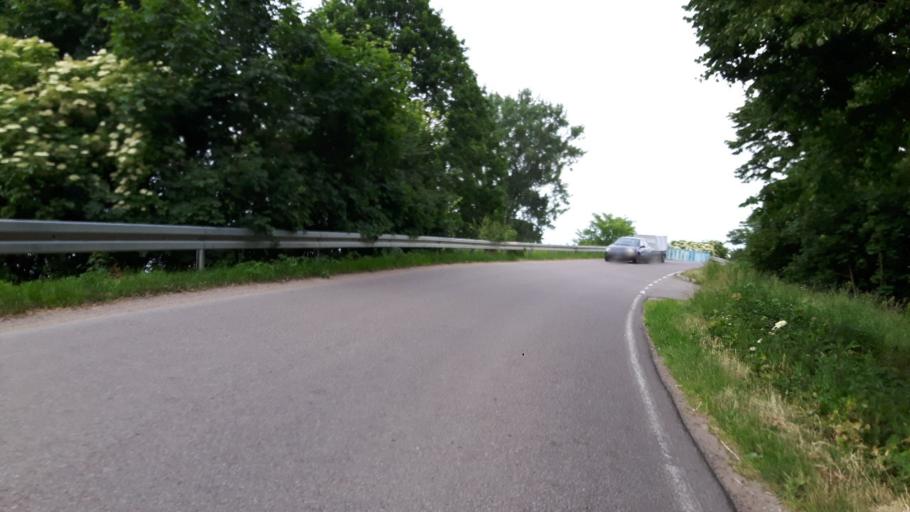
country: PL
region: Warmian-Masurian Voivodeship
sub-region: Powiat elblaski
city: Elblag
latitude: 54.1936
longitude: 19.3239
